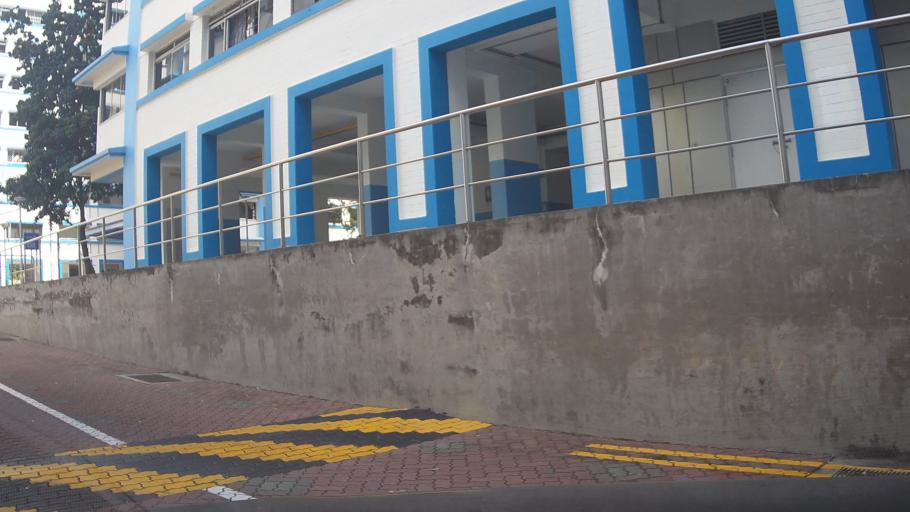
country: SG
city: Singapore
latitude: 1.3652
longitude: 103.9588
